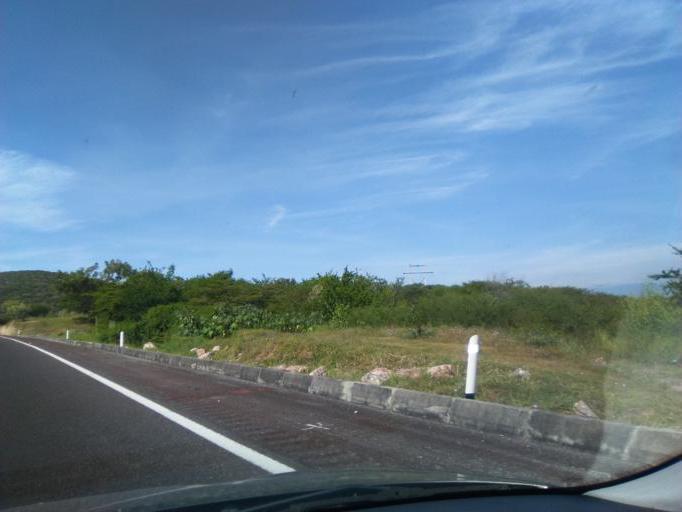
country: MX
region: Guerrero
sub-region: Huitzuco de los Figueroa
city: Ciudad de Huitzuco
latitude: 18.1682
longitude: -99.2109
